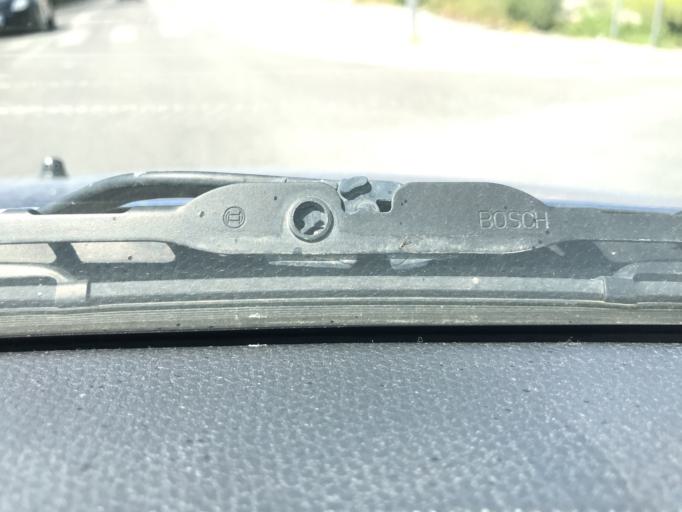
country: IT
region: Campania
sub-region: Provincia di Napoli
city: Calvizzano
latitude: 40.9117
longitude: 14.1891
